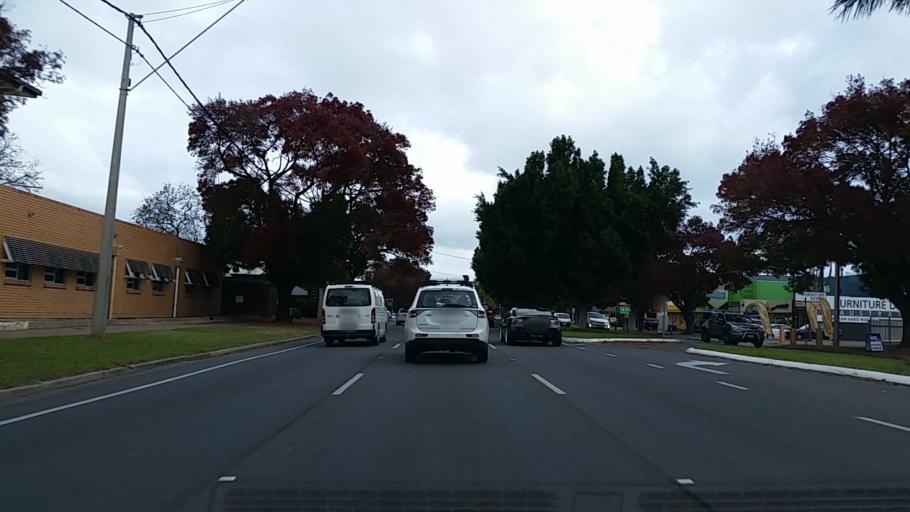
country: AU
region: South Australia
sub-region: Unley
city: Forestville
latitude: -34.9471
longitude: 138.5788
